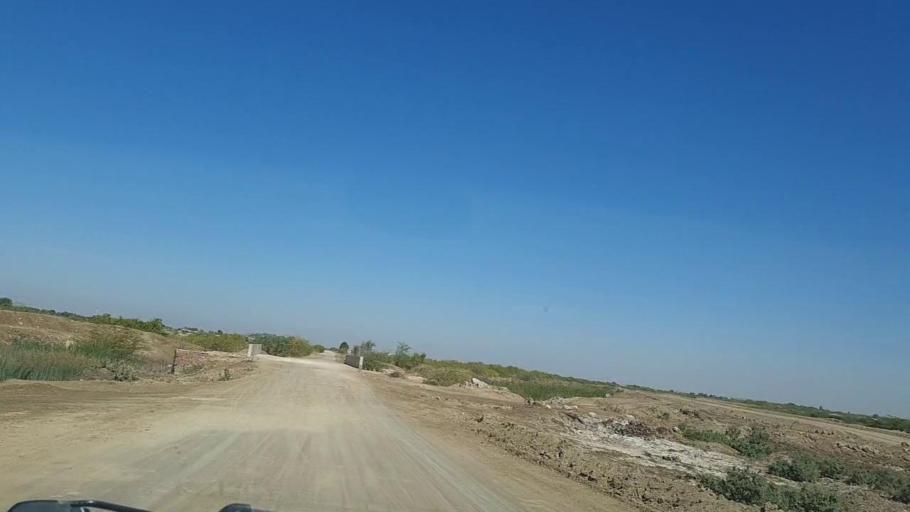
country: PK
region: Sindh
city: Dhoro Naro
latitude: 25.4764
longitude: 69.5272
